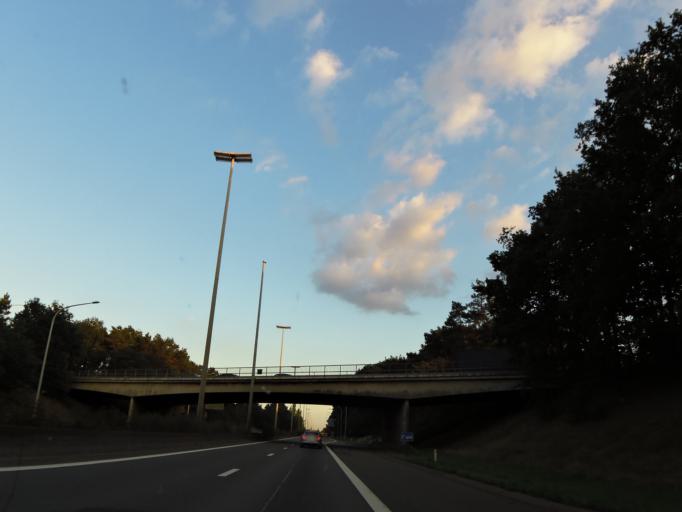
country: BE
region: Flanders
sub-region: Provincie Limburg
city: Beringen
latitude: 51.0424
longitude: 5.1845
